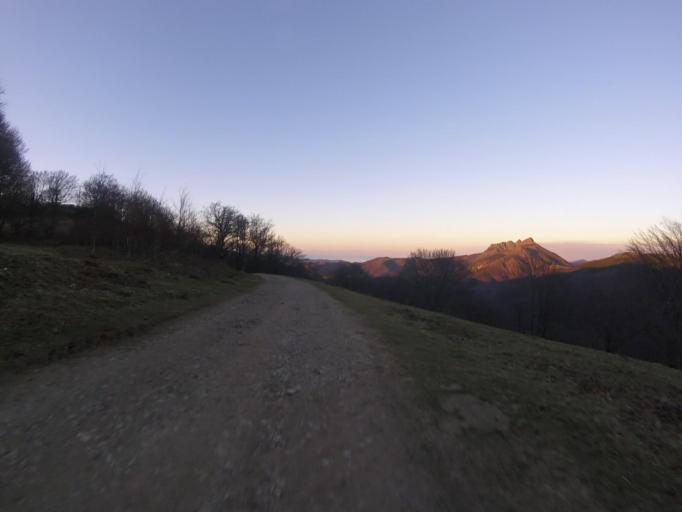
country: ES
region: Navarre
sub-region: Provincia de Navarra
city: Arano
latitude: 43.2527
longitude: -1.8246
